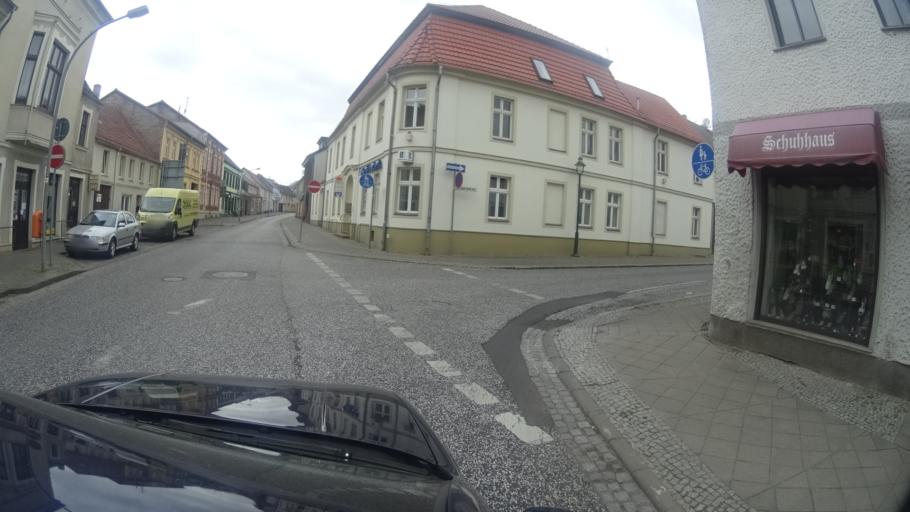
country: DE
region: Brandenburg
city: Fehrbellin
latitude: 52.8133
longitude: 12.7660
